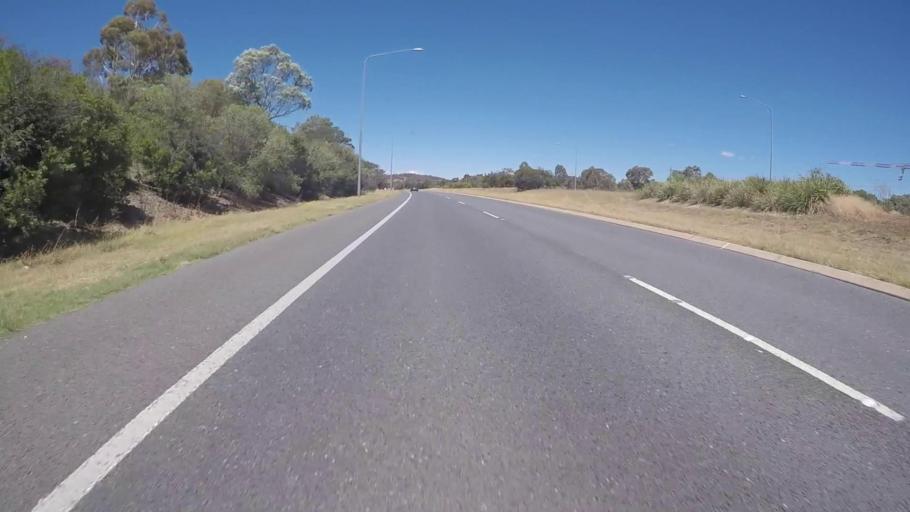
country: AU
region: Australian Capital Territory
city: Macarthur
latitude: -35.4195
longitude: 149.0761
